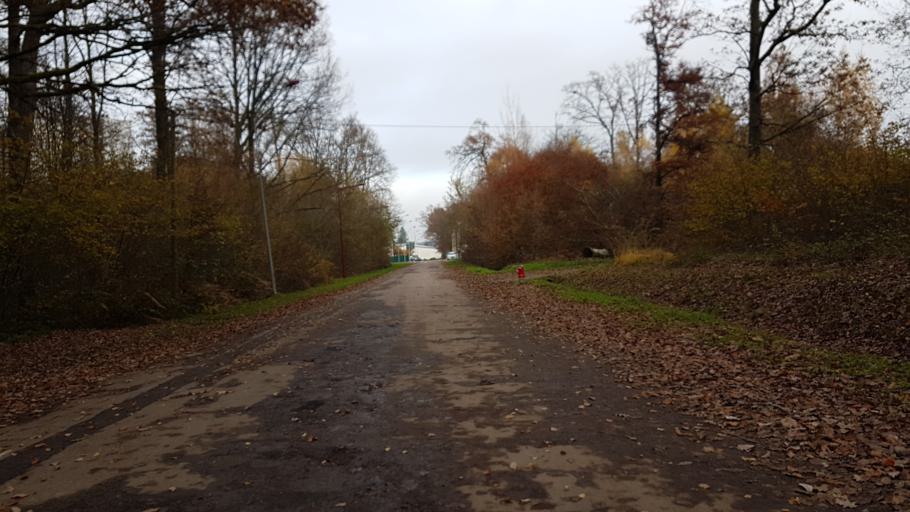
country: FR
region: Franche-Comte
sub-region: Departement de la Haute-Saone
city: Luxeuil-les-Bains
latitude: 47.8108
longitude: 6.3561
